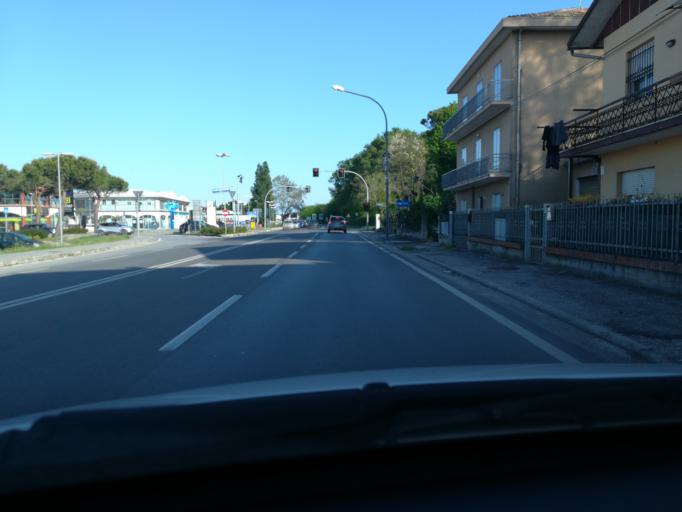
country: IT
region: Emilia-Romagna
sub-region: Provincia di Rimini
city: Misano Adriatico
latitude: 43.9794
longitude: 12.6857
